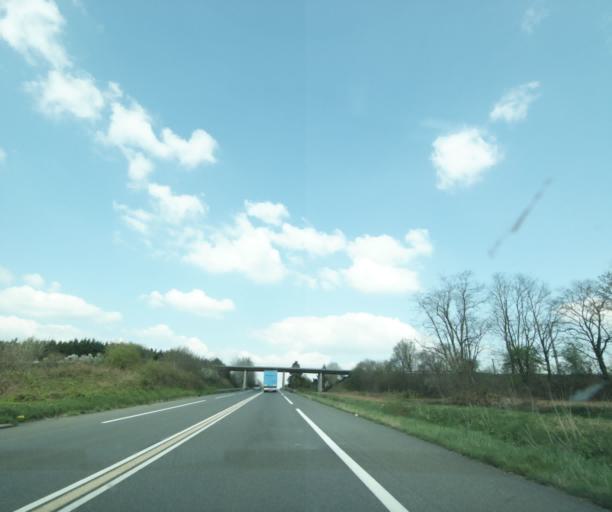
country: FR
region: Auvergne
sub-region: Departement de l'Allier
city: Montmarault
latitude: 46.3424
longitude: 2.9868
